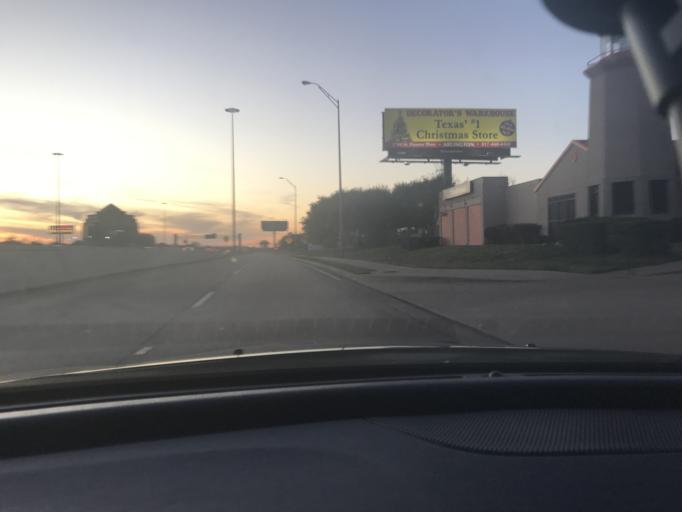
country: US
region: Texas
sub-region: Tarrant County
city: Arlington
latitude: 32.7603
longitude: -97.1071
